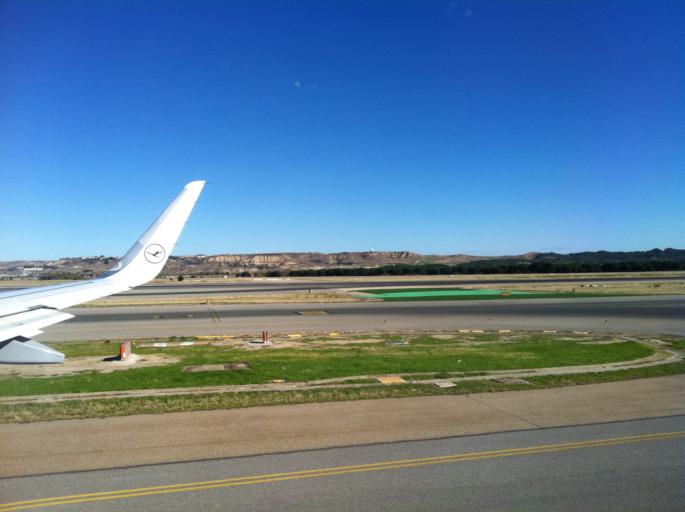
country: ES
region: Madrid
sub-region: Provincia de Madrid
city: Barajas de Madrid
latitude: 40.4766
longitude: -3.5715
